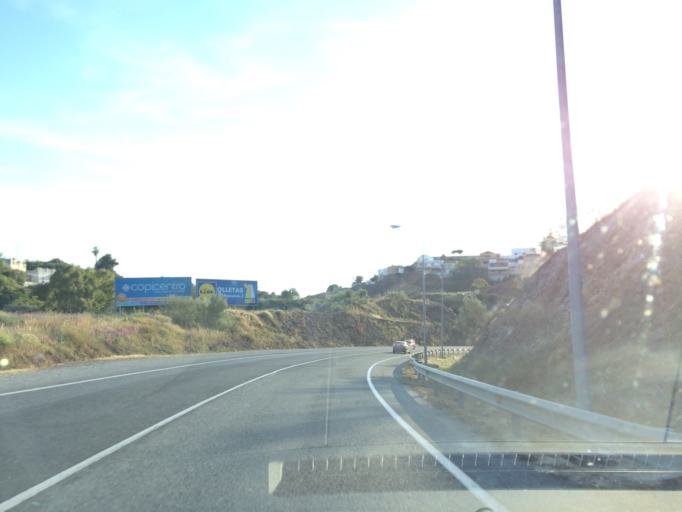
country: ES
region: Andalusia
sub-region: Provincia de Malaga
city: Malaga
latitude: 36.7404
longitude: -4.4094
